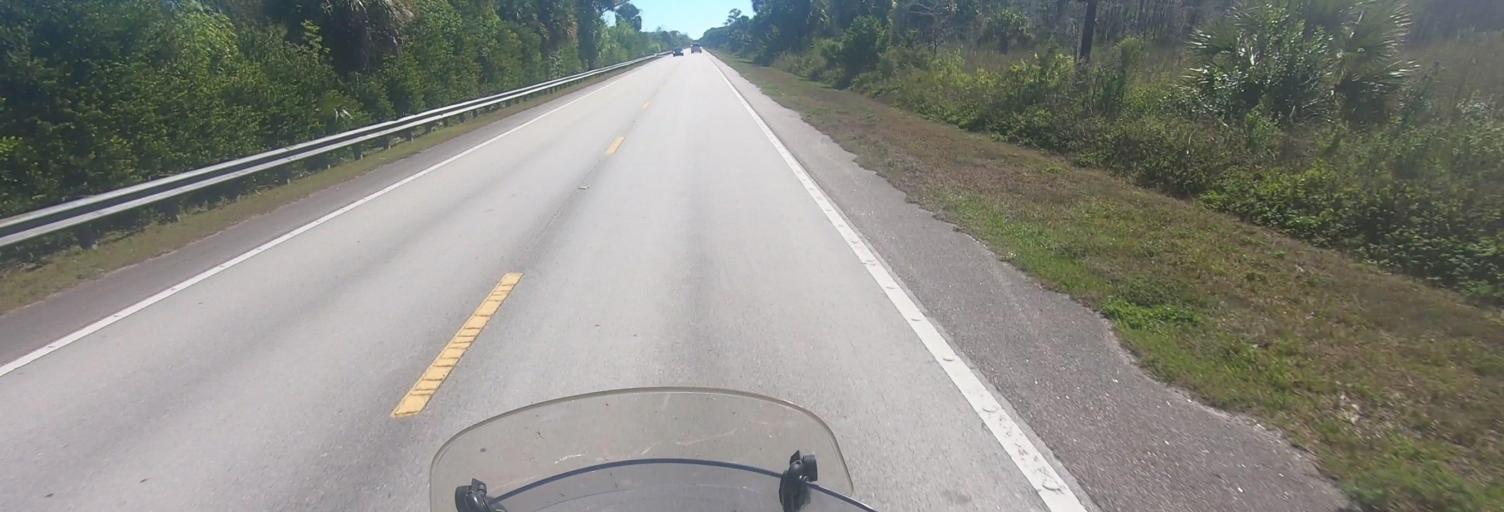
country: US
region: Florida
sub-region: Collier County
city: Marco
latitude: 25.8714
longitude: -81.1775
